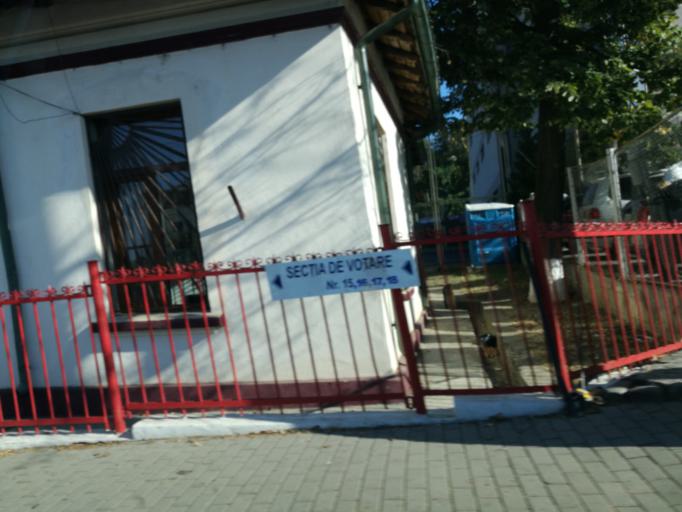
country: RO
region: Iasi
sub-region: Municipiul Iasi
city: Iasi
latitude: 47.1731
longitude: 27.5616
